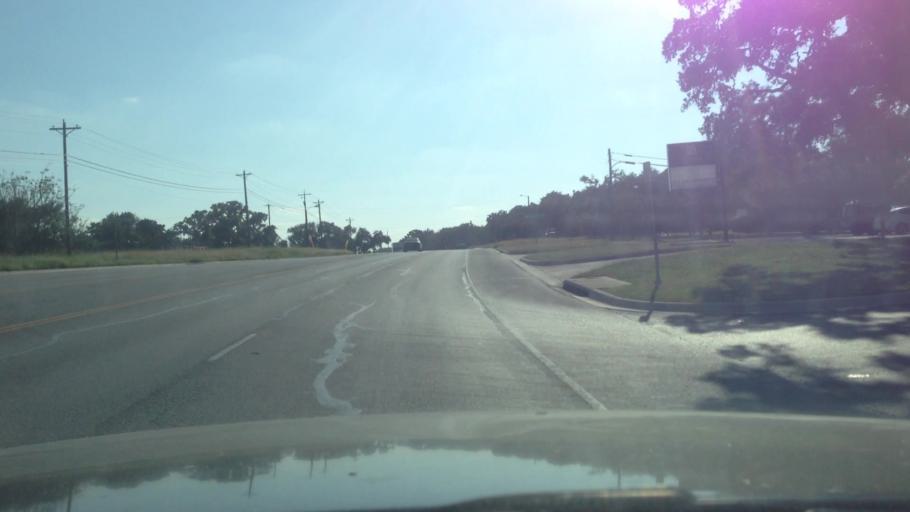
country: US
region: Texas
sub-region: Hays County
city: San Marcos
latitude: 29.8523
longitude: -97.9737
